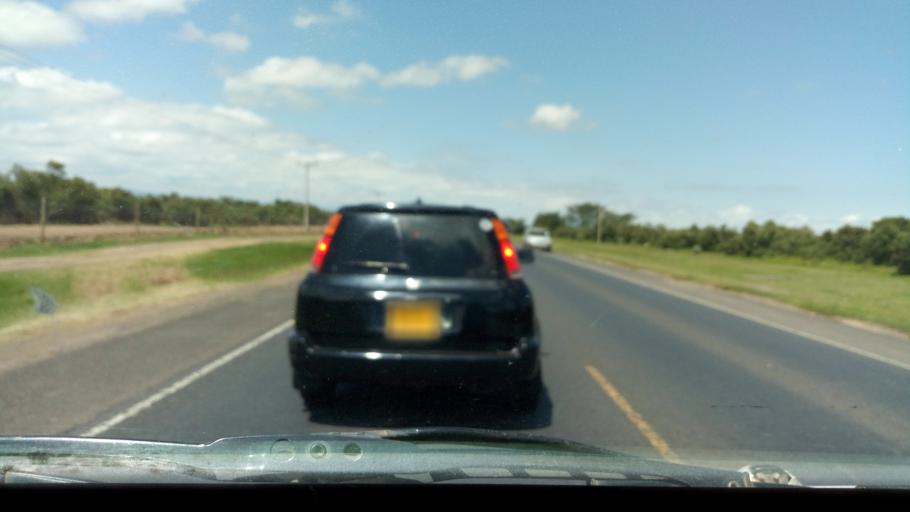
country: KE
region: Nakuru
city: Naivasha
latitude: -0.5594
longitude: 36.3525
